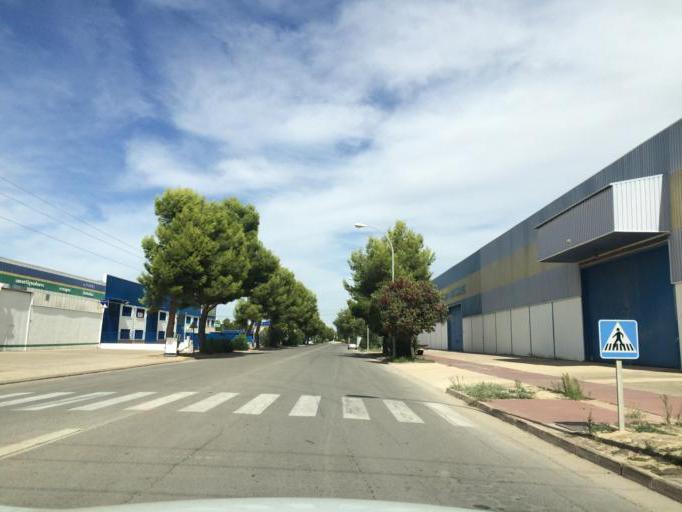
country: ES
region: Castille-La Mancha
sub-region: Provincia de Albacete
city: Albacete
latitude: 39.0151
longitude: -1.8866
